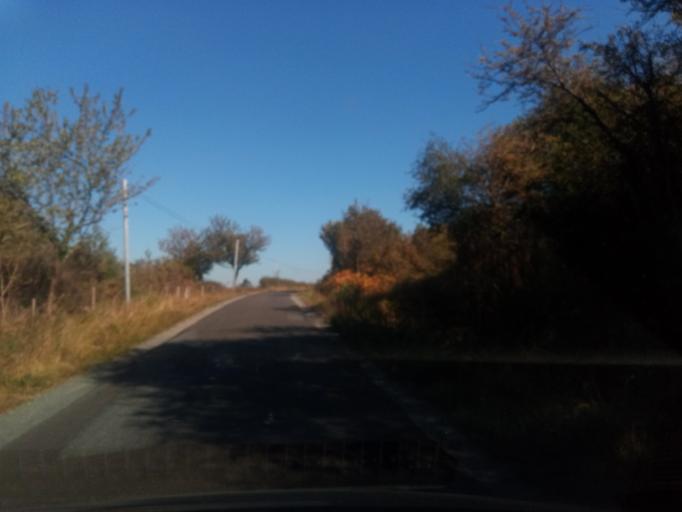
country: FR
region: Poitou-Charentes
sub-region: Departement de la Vienne
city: Montmorillon
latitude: 46.4260
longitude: 0.8303
